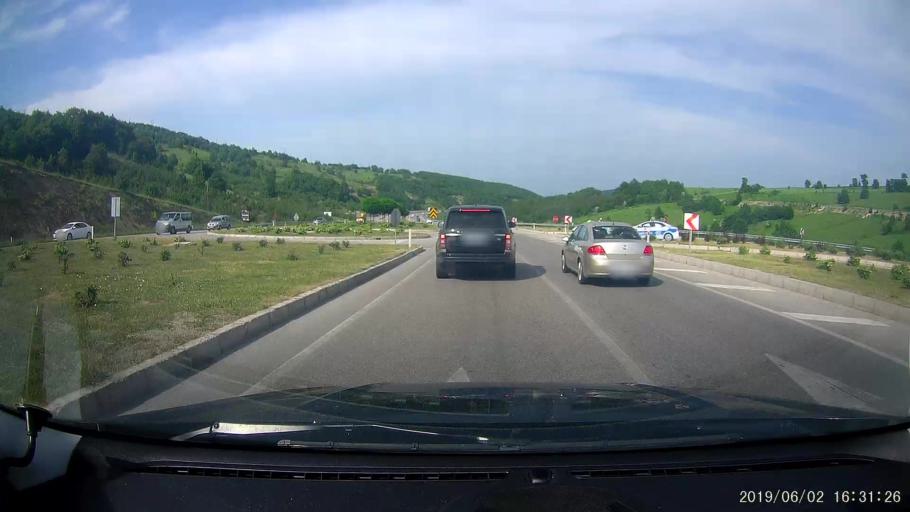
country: TR
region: Samsun
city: Ladik
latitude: 41.0321
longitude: 35.9012
